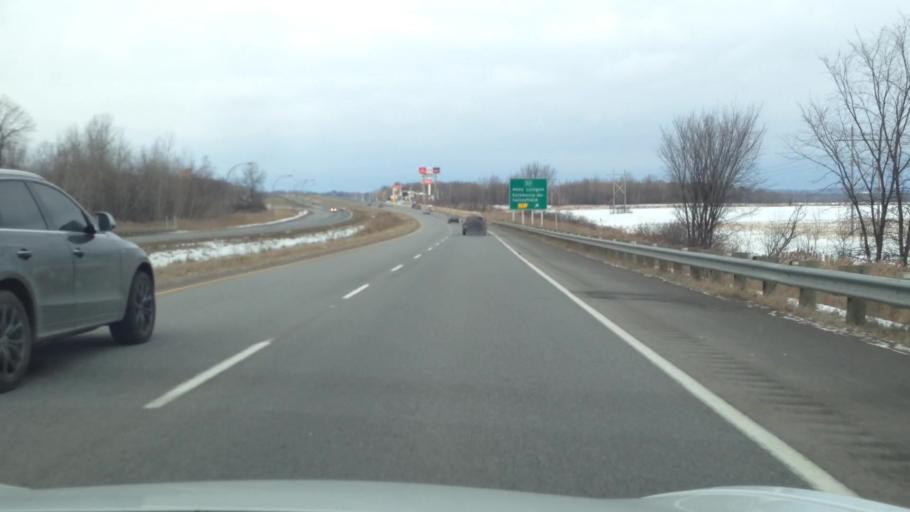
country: CA
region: Quebec
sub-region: Monteregie
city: Hudson
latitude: 45.4563
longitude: -74.2191
